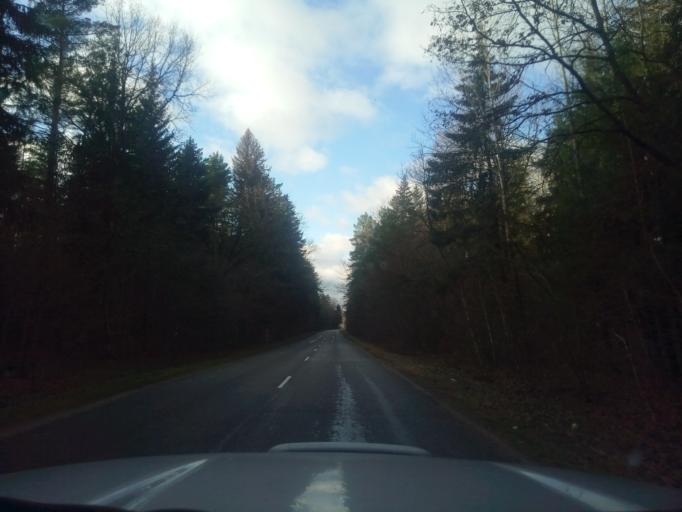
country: BY
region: Minsk
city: Kapyl'
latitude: 53.1753
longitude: 26.9905
